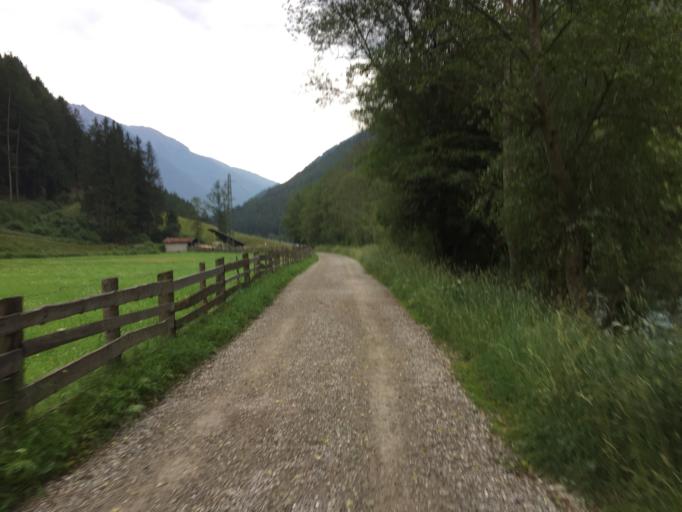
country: IT
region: Trentino-Alto Adige
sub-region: Bolzano
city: Molini di Tures
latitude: 46.9472
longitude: 11.9238
